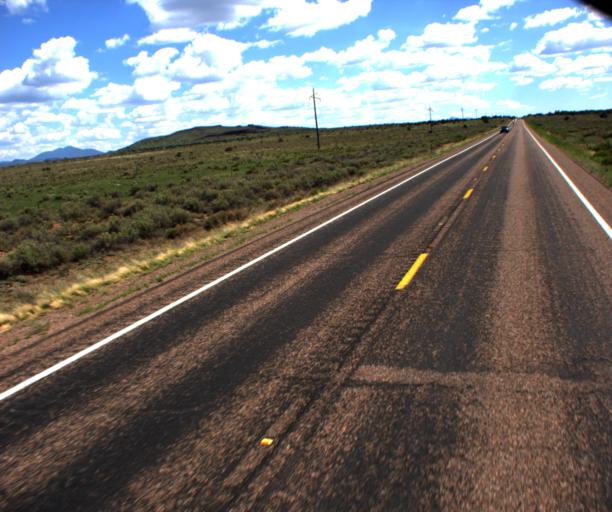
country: US
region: Arizona
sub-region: Coconino County
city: Williams
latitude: 35.5695
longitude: -112.1554
